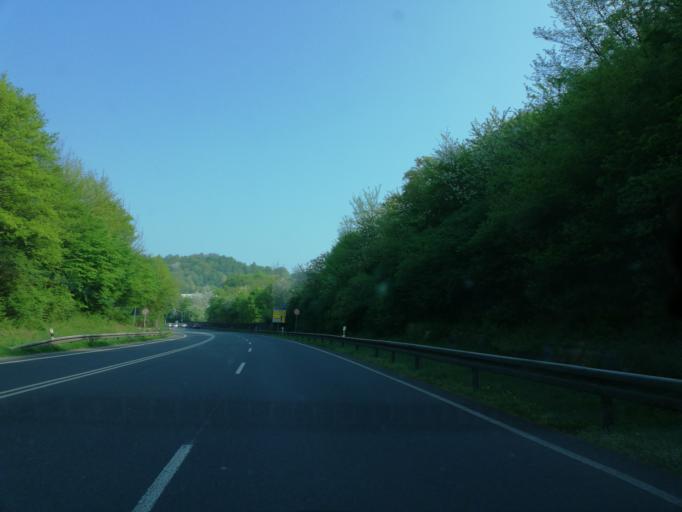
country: DE
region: North Rhine-Westphalia
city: Herdecke
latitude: 51.4057
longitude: 7.4350
